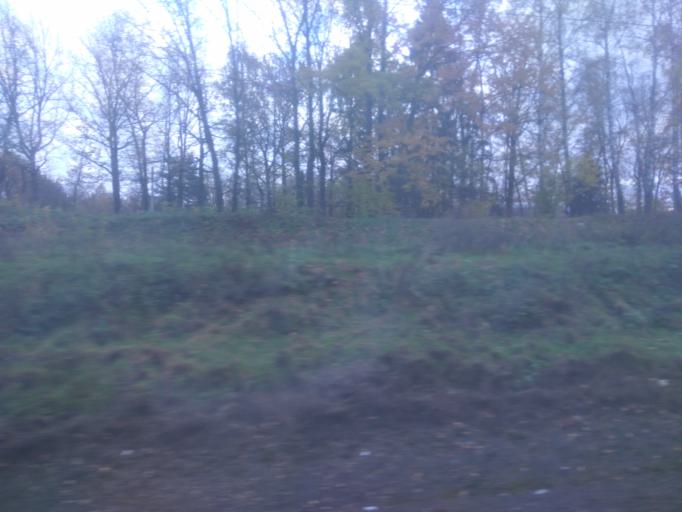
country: RU
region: Moskovskaya
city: Kokoshkino
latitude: 55.5976
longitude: 37.1674
